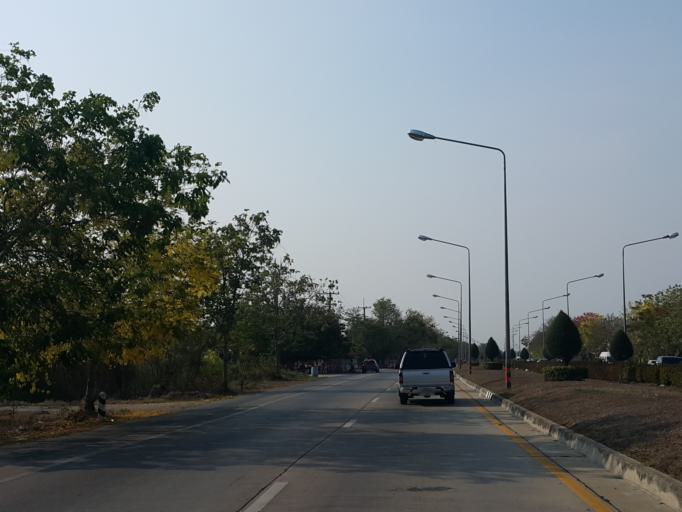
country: TH
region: Suphan Buri
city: Sam Chuk
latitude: 14.7639
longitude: 100.0938
